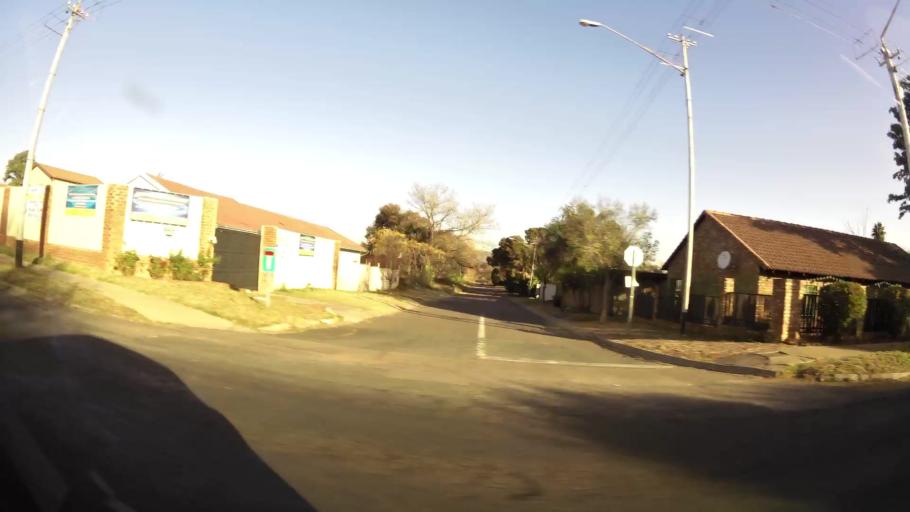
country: ZA
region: Gauteng
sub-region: City of Tshwane Metropolitan Municipality
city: Pretoria
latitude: -25.7018
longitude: 28.2107
